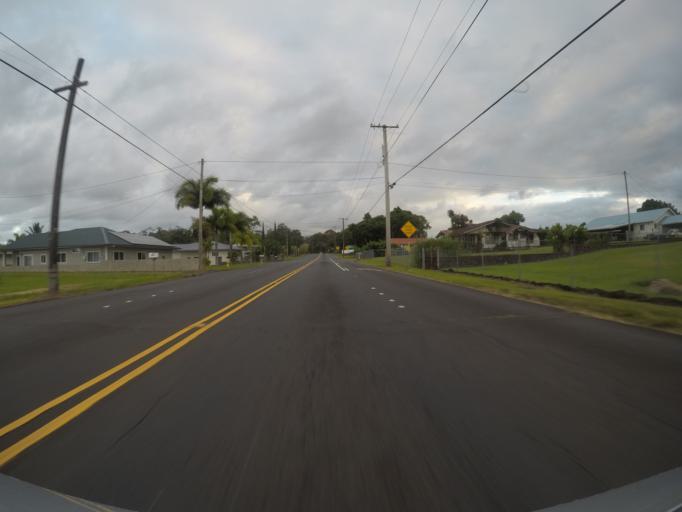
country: US
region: Hawaii
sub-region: Hawaii County
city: Hilo
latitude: 19.6764
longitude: -155.0669
